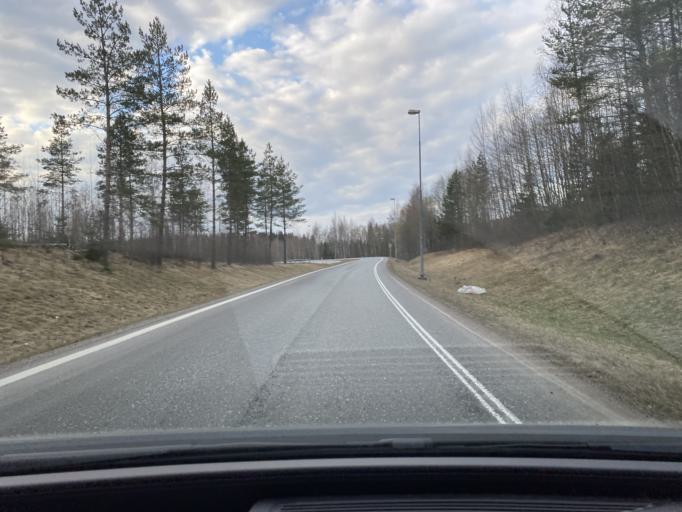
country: FI
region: Uusimaa
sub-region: Helsinki
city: Hyvinge
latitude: 60.5656
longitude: 24.8213
